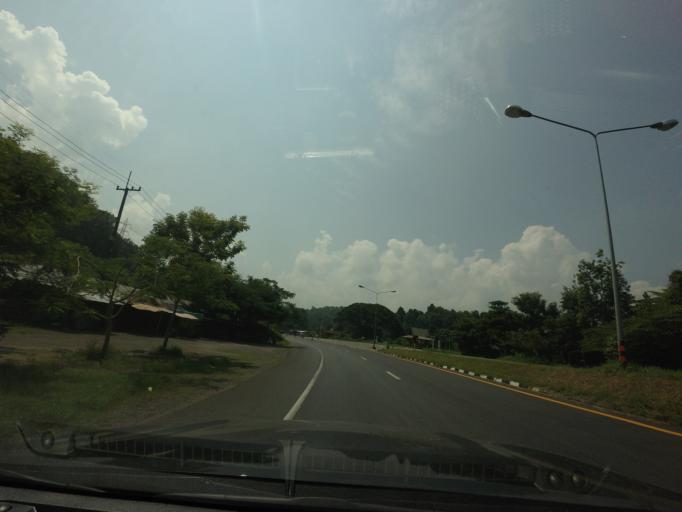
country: TH
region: Phrae
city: Den Chai
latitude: 17.8836
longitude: 100.0464
